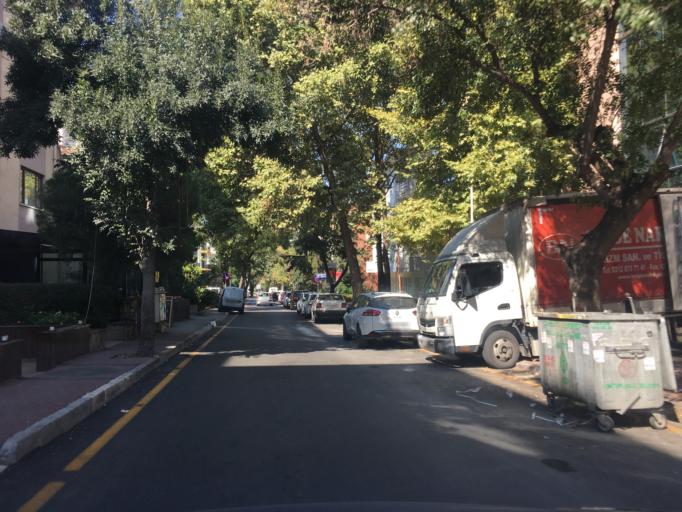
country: TR
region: Ankara
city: Cankaya
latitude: 39.8966
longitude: 32.8563
